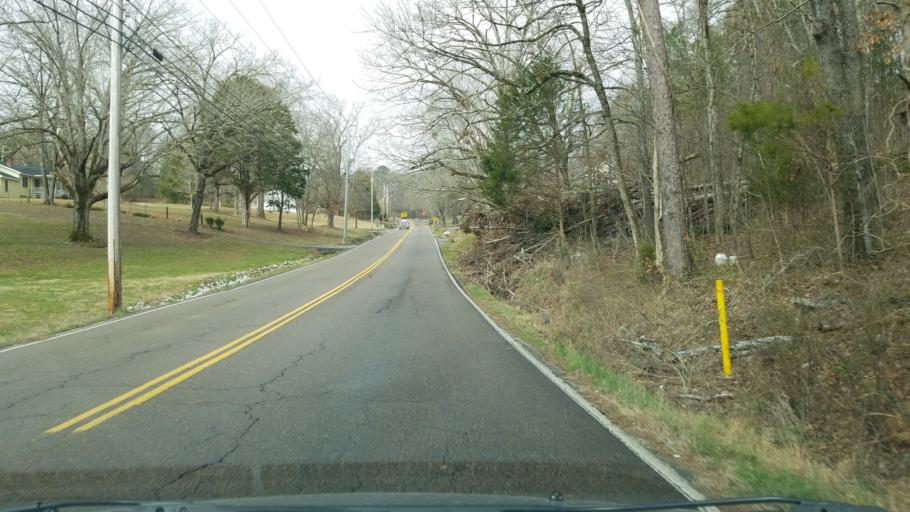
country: US
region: Tennessee
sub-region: Hamilton County
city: East Brainerd
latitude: 34.9996
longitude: -85.1075
